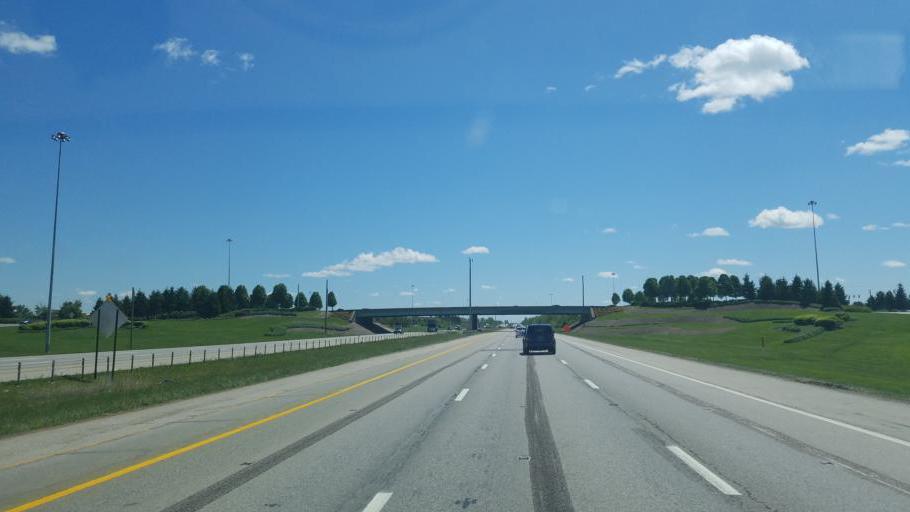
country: US
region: Ohio
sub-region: Franklin County
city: Dublin
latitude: 40.0777
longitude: -83.1363
